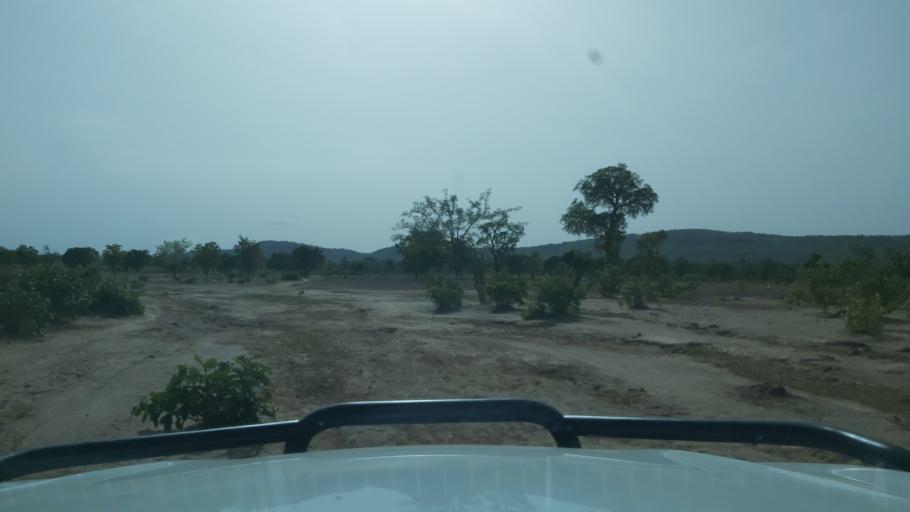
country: ML
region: Koulikoro
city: Koulikoro
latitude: 13.1757
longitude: -7.7421
